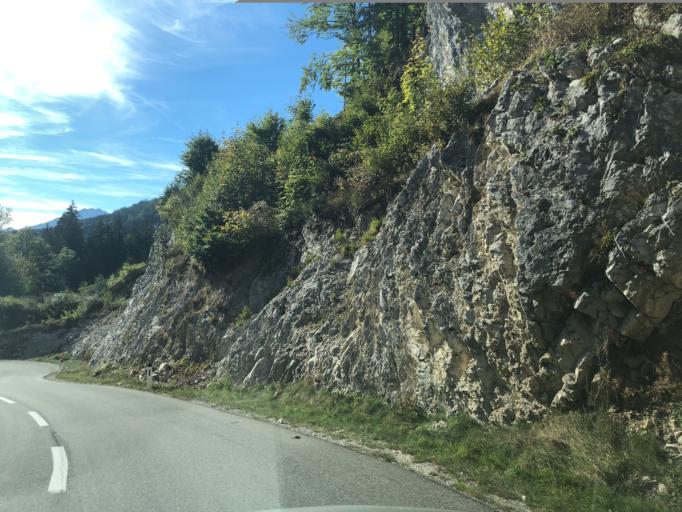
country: AT
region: Tyrol
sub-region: Politischer Bezirk Reutte
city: Ehenbichl
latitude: 47.4597
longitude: 10.7194
